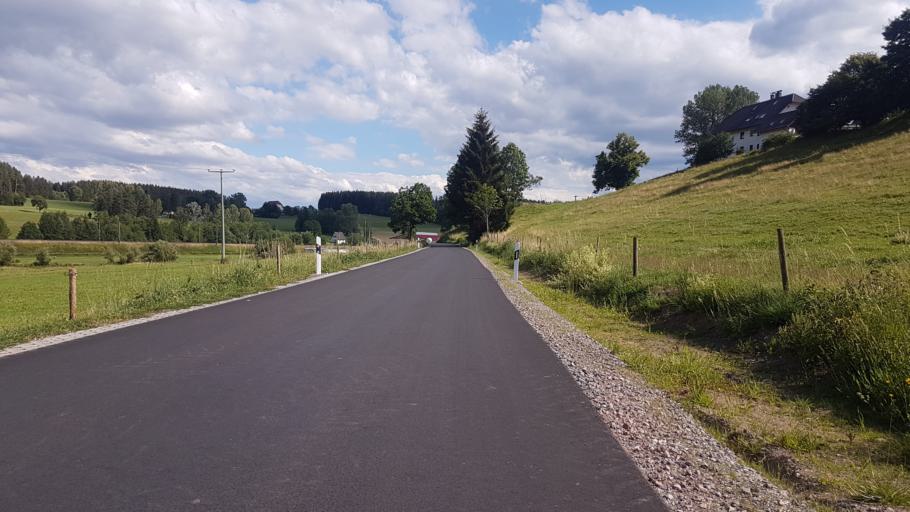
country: DE
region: Baden-Wuerttemberg
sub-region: Freiburg Region
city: Konigsfeld im Schwarzwald
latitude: 48.1147
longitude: 8.3937
